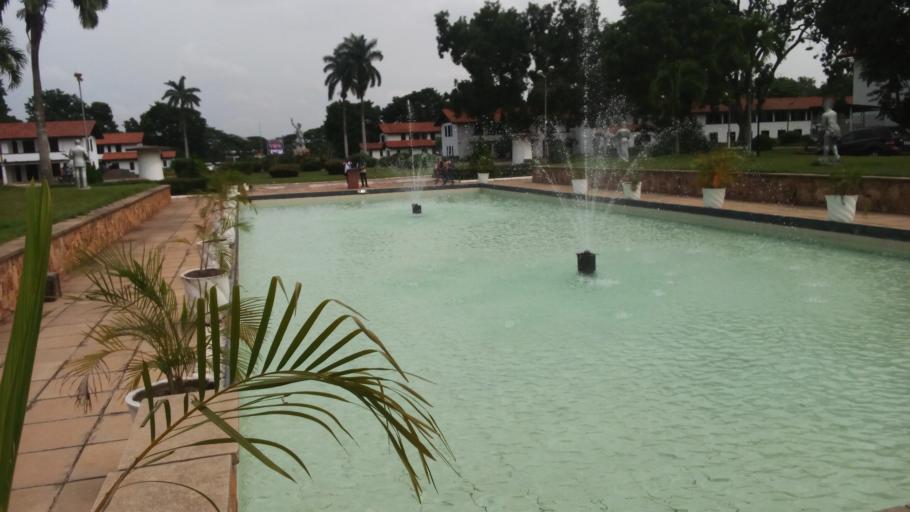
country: GH
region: Greater Accra
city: Medina Estates
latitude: 5.6513
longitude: -0.1871
